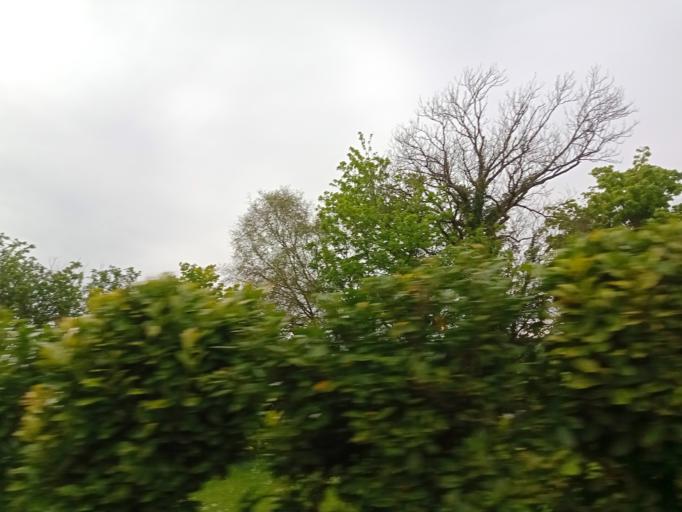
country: IE
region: Leinster
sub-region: Kilkenny
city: Ballyragget
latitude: 52.7183
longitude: -7.4812
